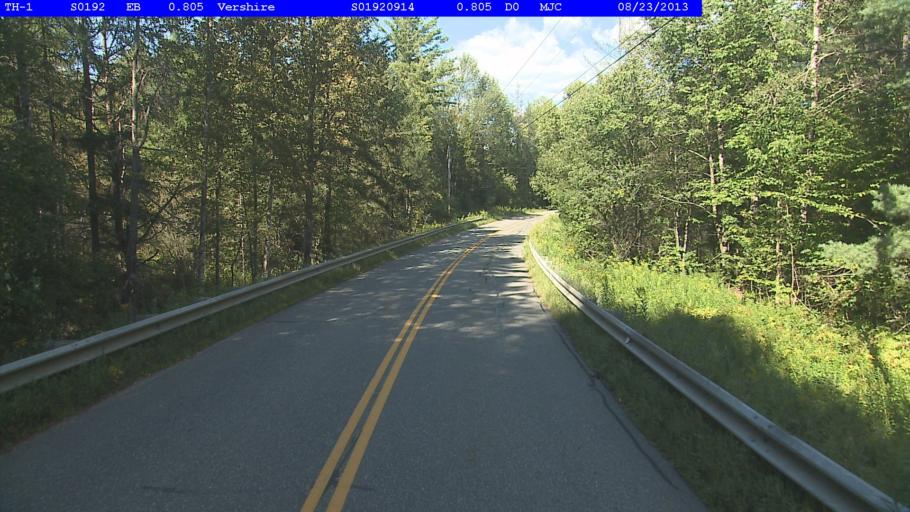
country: US
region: Vermont
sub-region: Orange County
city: Chelsea
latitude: 43.9982
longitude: -72.3644
